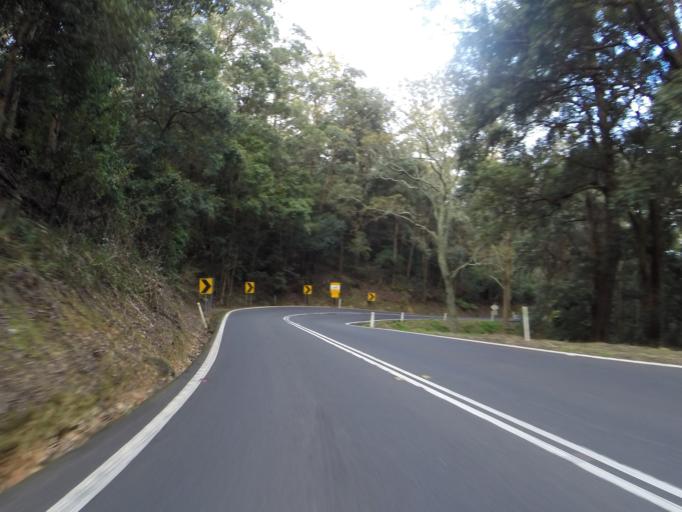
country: AU
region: New South Wales
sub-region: Shellharbour
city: Calderwood
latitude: -34.5717
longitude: 150.6704
